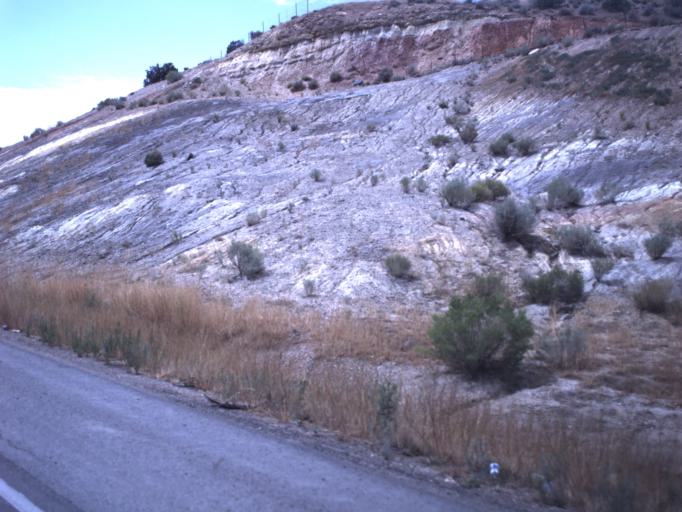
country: US
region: Utah
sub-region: Uintah County
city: Maeser
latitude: 40.4160
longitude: -109.5828
